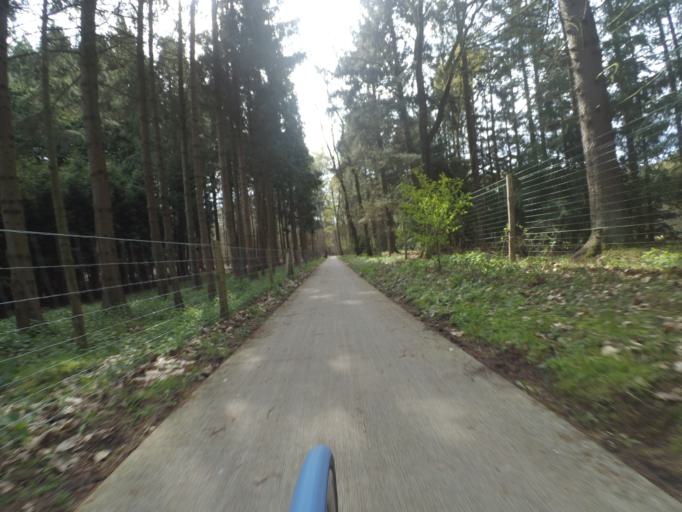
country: NL
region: Gelderland
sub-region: Gemeente Nunspeet
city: Nunspeet
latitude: 52.3471
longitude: 5.8050
